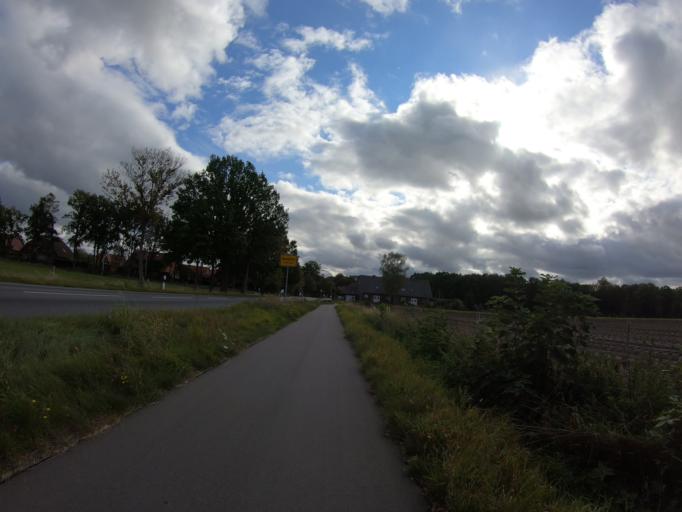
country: DE
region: Lower Saxony
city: Wasbuttel
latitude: 52.4188
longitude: 10.5904
